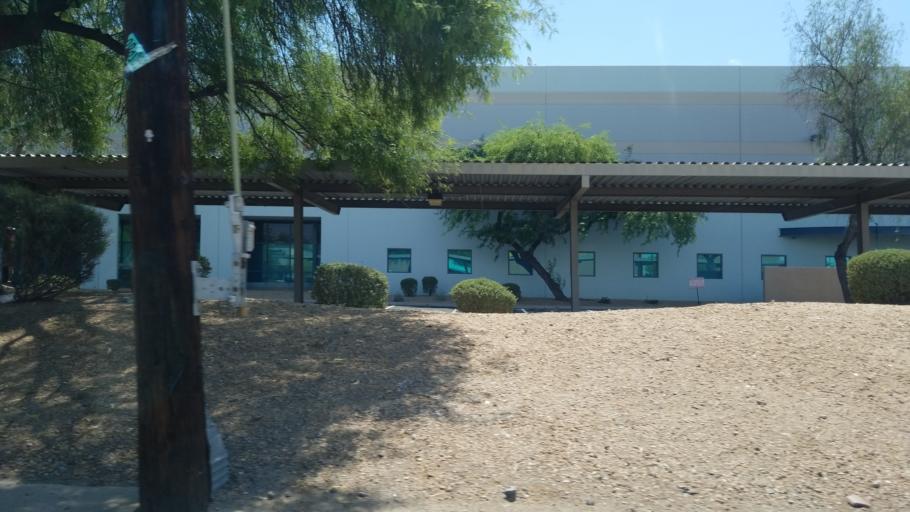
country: US
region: Arizona
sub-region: Maricopa County
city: Phoenix
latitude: 33.4505
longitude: -112.1517
